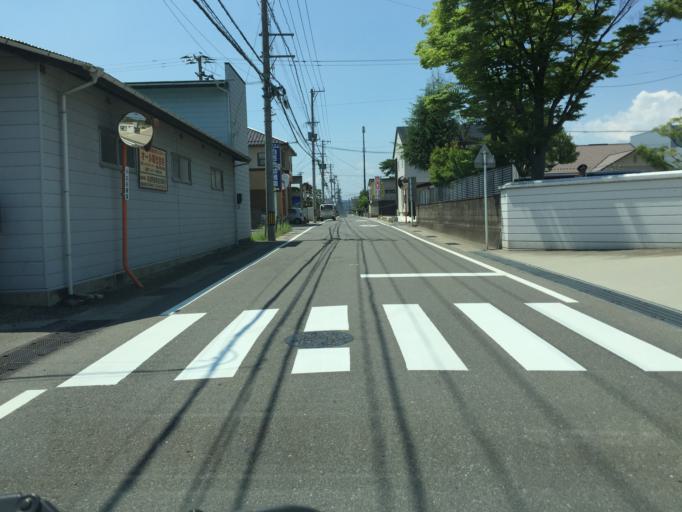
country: JP
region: Fukushima
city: Fukushima-shi
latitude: 37.7471
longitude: 140.4481
